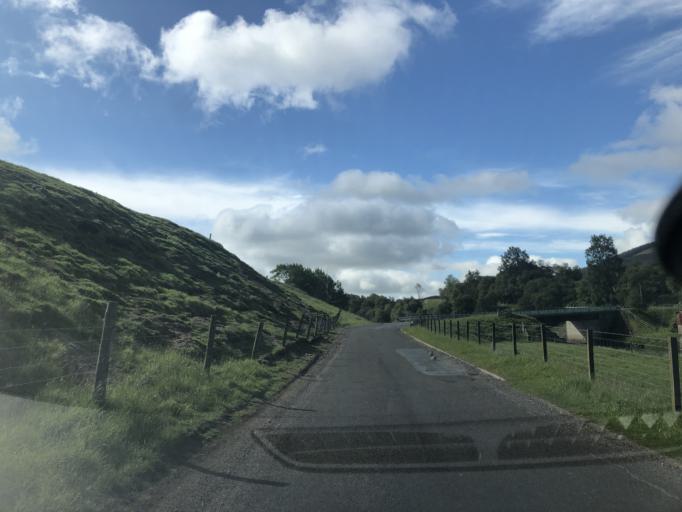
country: GB
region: Scotland
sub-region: Angus
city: Kirriemuir
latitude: 56.7759
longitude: -3.0276
